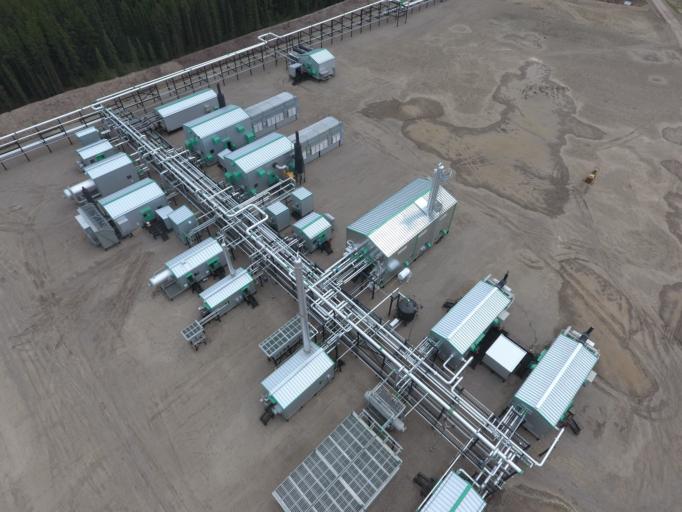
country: CA
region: Alberta
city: Edson
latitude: 52.8414
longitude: -116.0410
